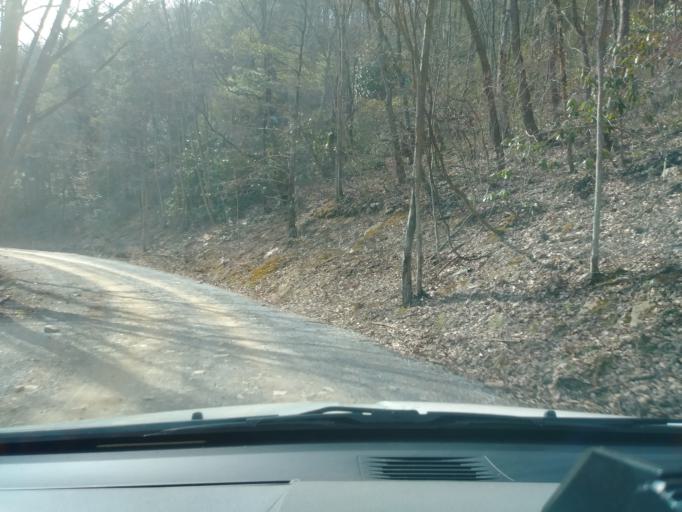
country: US
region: Tennessee
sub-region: Greene County
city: Tusculum
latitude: 36.0335
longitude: -82.7261
